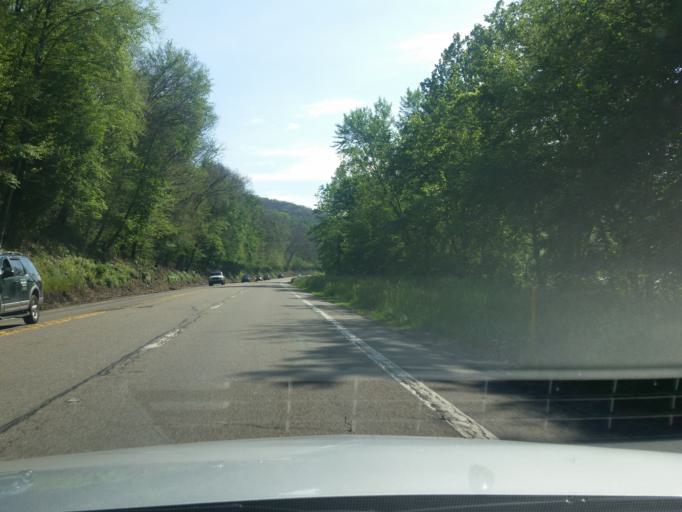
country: US
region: Pennsylvania
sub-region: Luzerne County
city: Nanticoke
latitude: 41.2193
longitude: -76.0293
